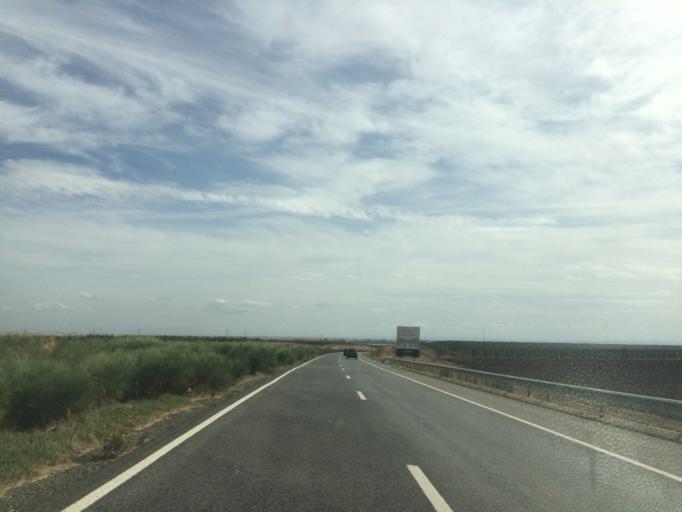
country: MA
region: Meknes-Tafilalet
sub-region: Meknes
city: Meknes
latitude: 33.8930
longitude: -5.6723
